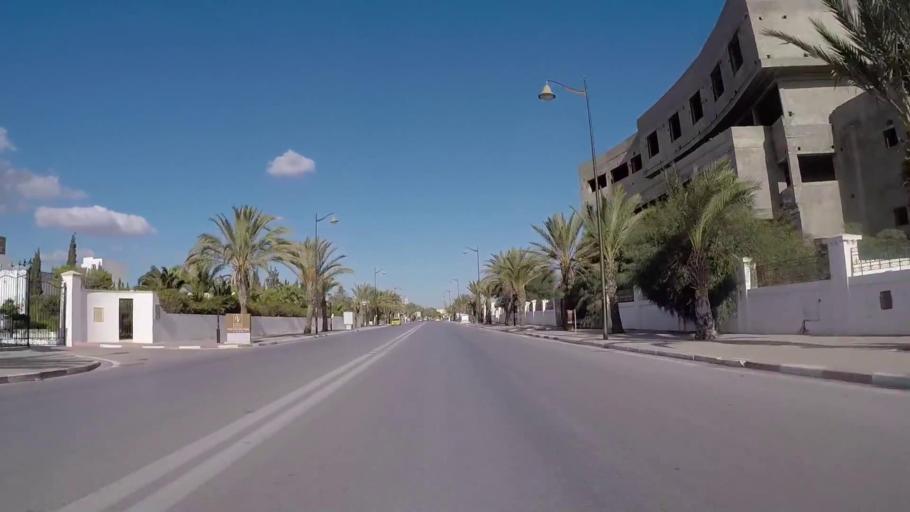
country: TN
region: Nabul
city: Al Hammamat
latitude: 36.3628
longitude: 10.5319
